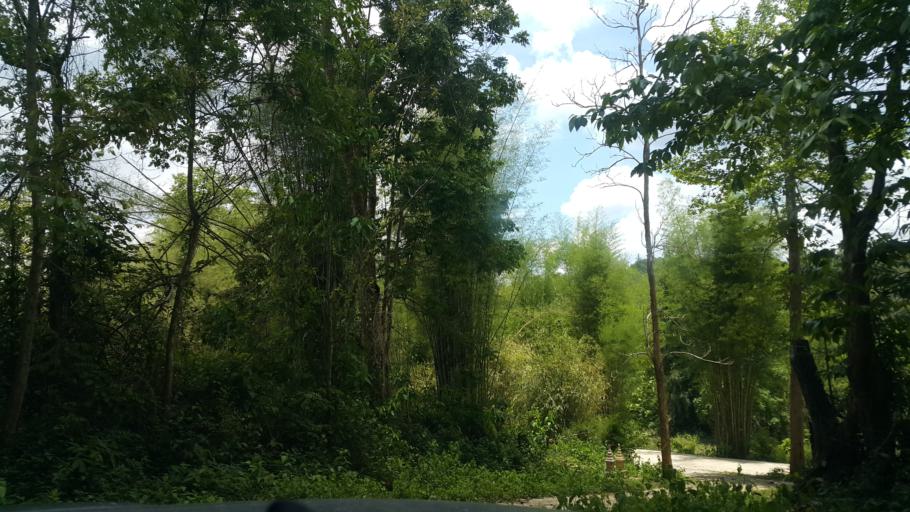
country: TH
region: Phayao
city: Phayao
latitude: 19.1739
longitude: 99.7854
